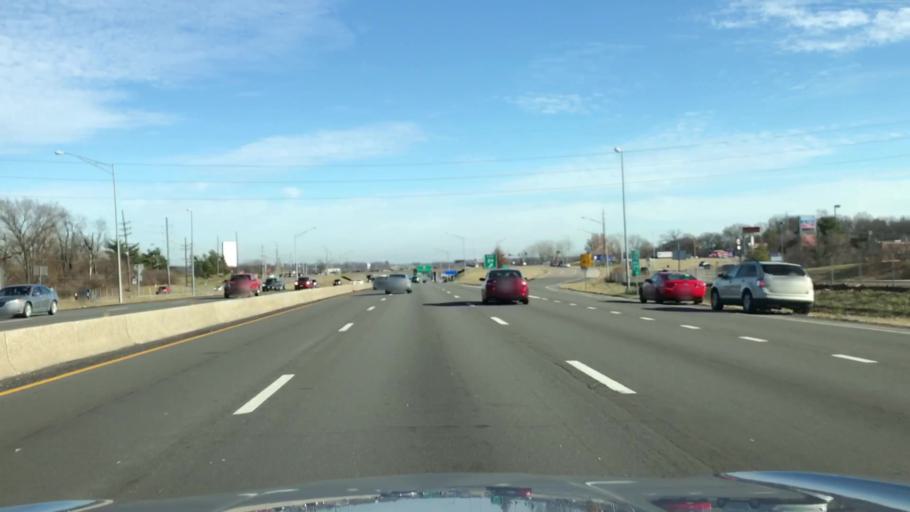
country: US
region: Missouri
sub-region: Saint Louis County
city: Dellwood
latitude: 38.7713
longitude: -90.2848
